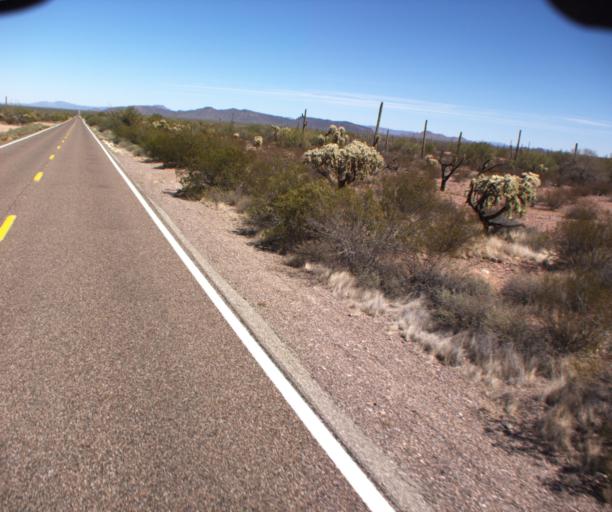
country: MX
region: Sonora
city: Sonoyta
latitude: 32.1041
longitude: -112.7707
